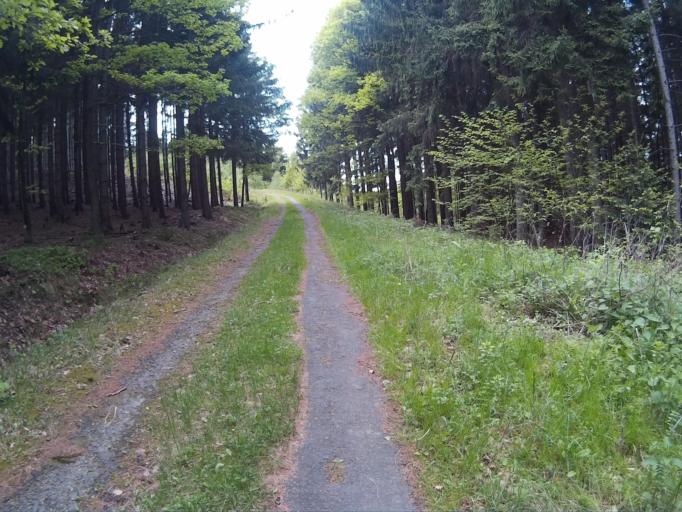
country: HU
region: Vas
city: Koszeg
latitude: 47.3723
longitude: 16.4888
